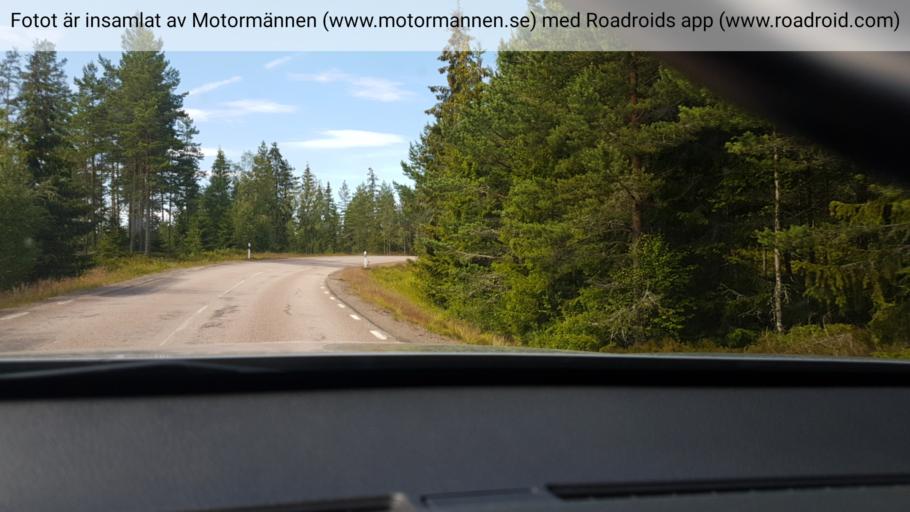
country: SE
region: Vaermland
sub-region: Sunne Kommun
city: Sunne
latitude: 59.8667
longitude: 13.3121
